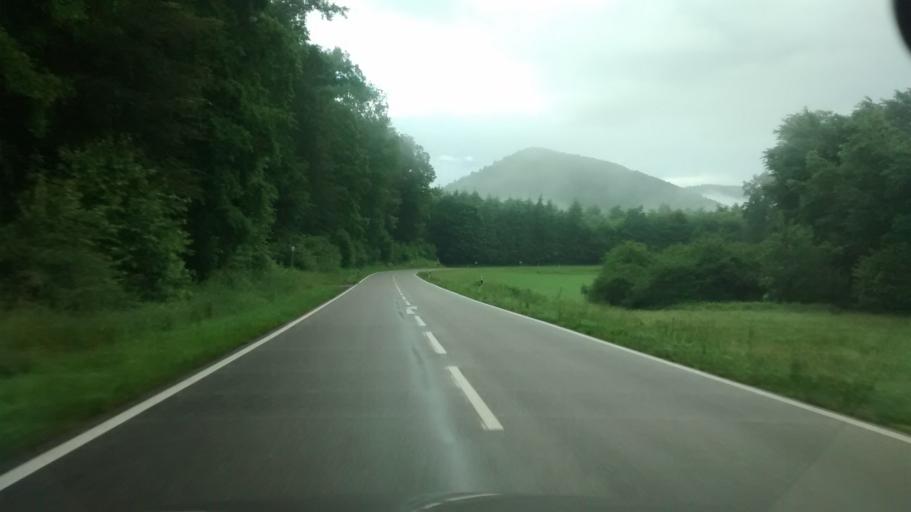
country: DE
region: Rheinland-Pfalz
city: Oberschlettenbach
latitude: 49.1220
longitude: 7.8567
